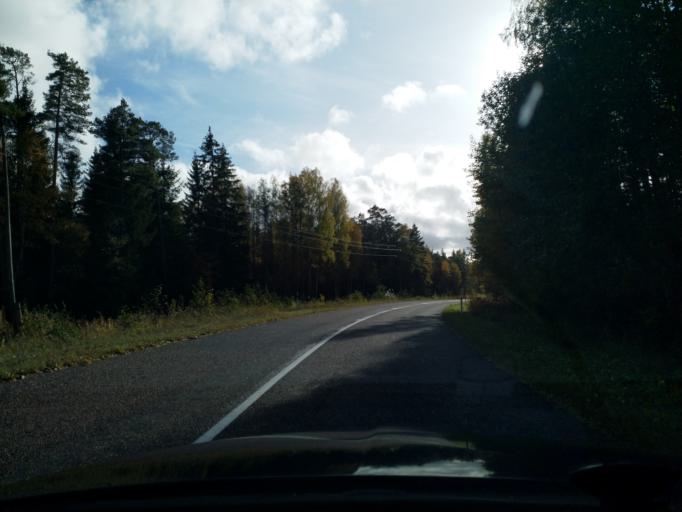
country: LV
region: Dundaga
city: Dundaga
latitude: 57.6443
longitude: 22.2646
